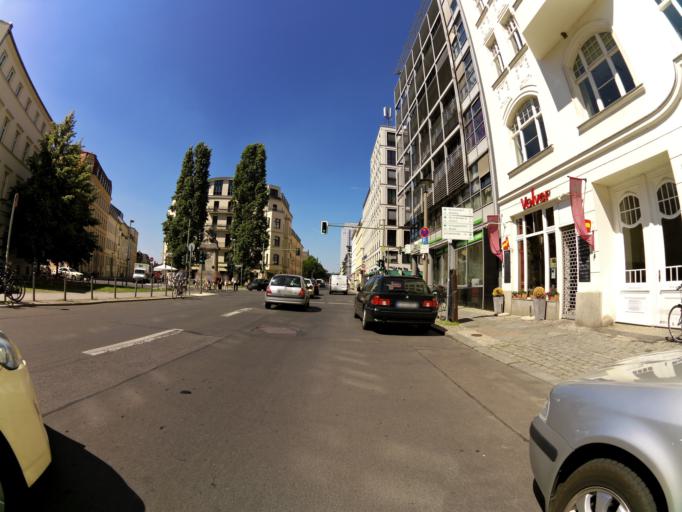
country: DE
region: Berlin
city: Tiergarten Bezirk
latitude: 52.5223
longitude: 13.3797
